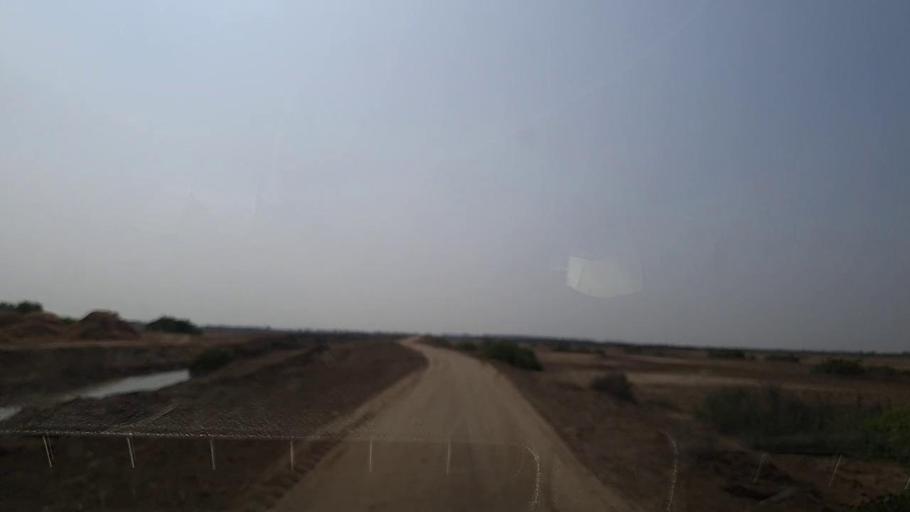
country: PK
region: Sindh
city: Mirpur Sakro
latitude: 24.5395
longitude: 67.7853
